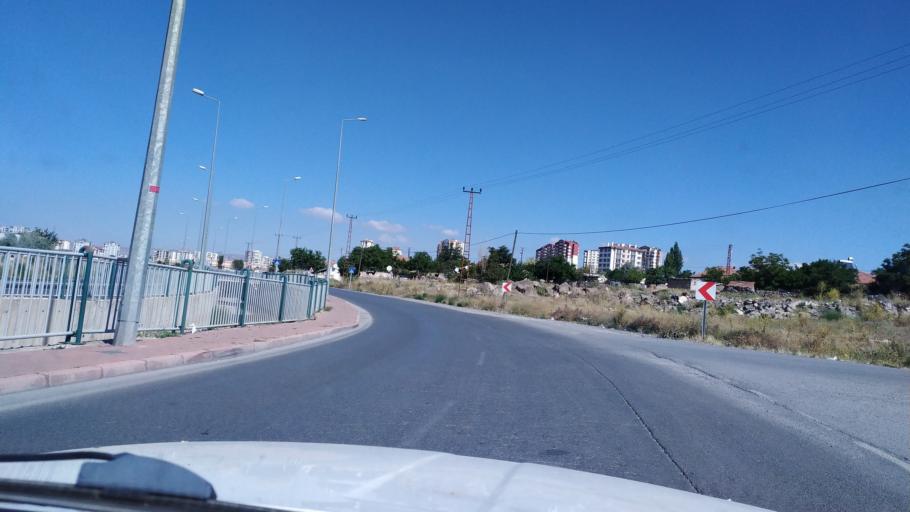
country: TR
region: Kayseri
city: Talas
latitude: 38.7328
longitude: 35.5492
